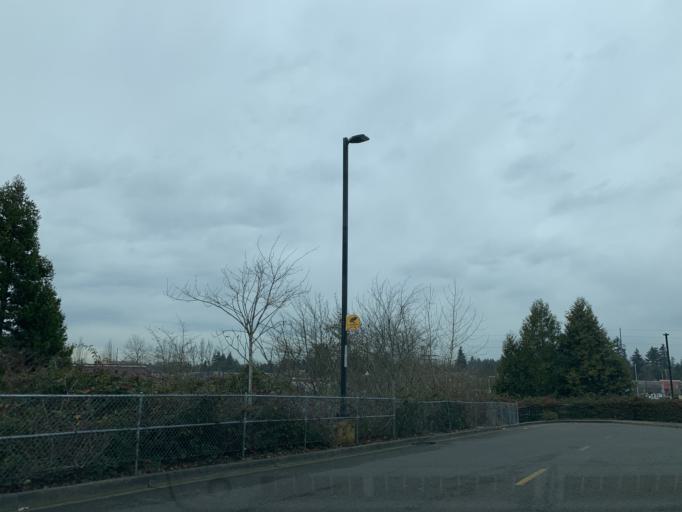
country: US
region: Washington
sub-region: King County
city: Federal Way
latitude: 47.3212
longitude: -122.3105
